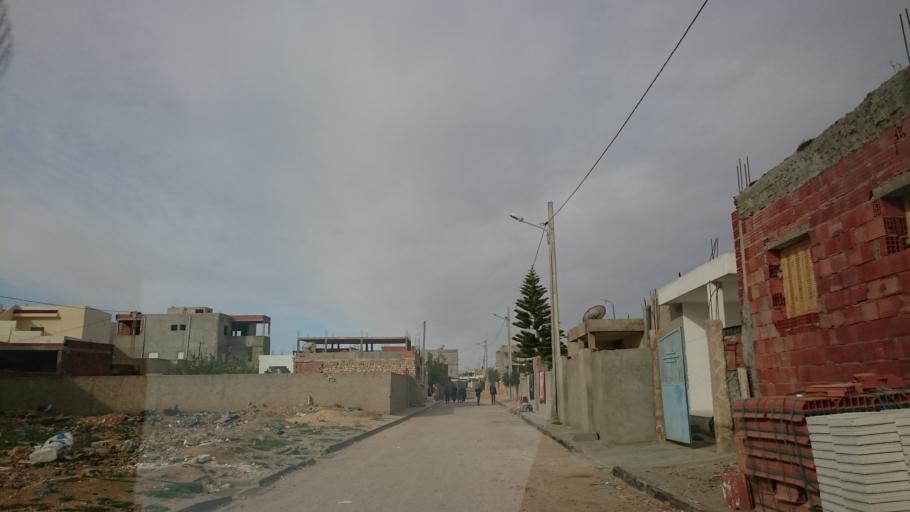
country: TN
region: Safaqis
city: Sfax
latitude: 34.7469
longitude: 10.5240
